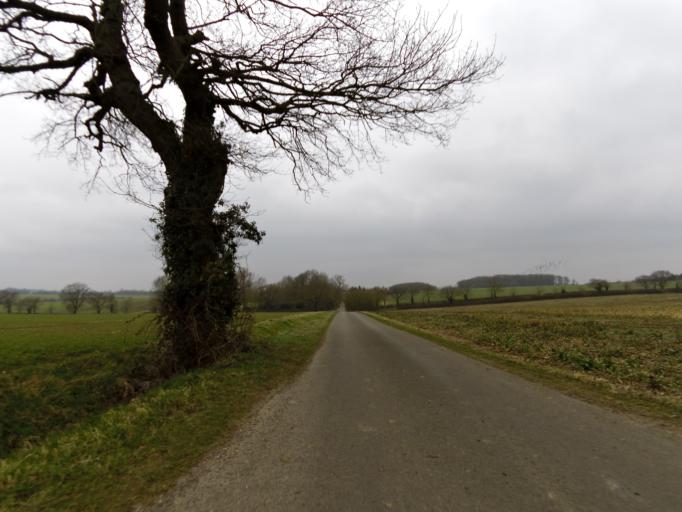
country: GB
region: England
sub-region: Suffolk
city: Framlingham
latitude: 52.2325
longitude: 1.3518
